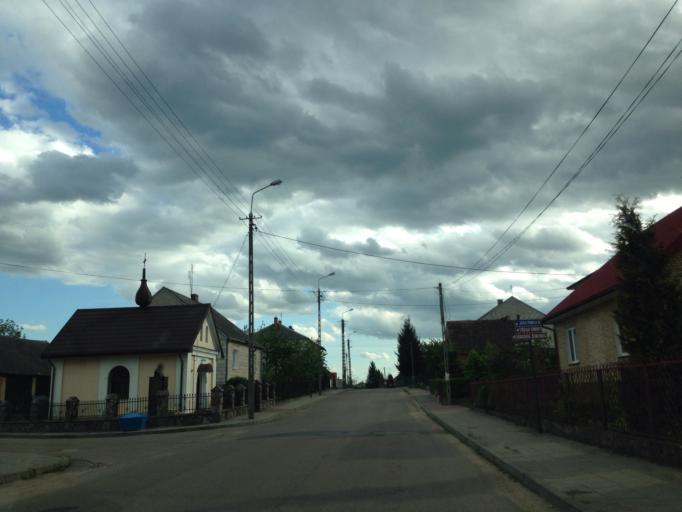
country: PL
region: Podlasie
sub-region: Powiat lomzynski
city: Wizna
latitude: 53.1988
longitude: 22.3848
